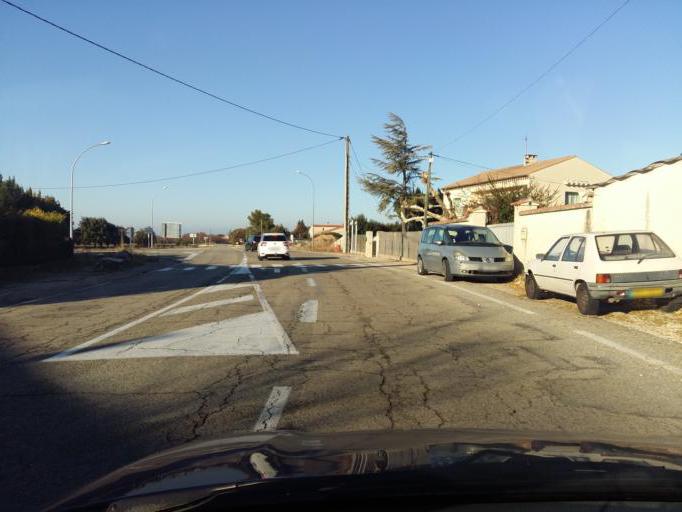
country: FR
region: Provence-Alpes-Cote d'Azur
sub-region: Departement du Vaucluse
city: Valreas
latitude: 44.3868
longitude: 4.9773
